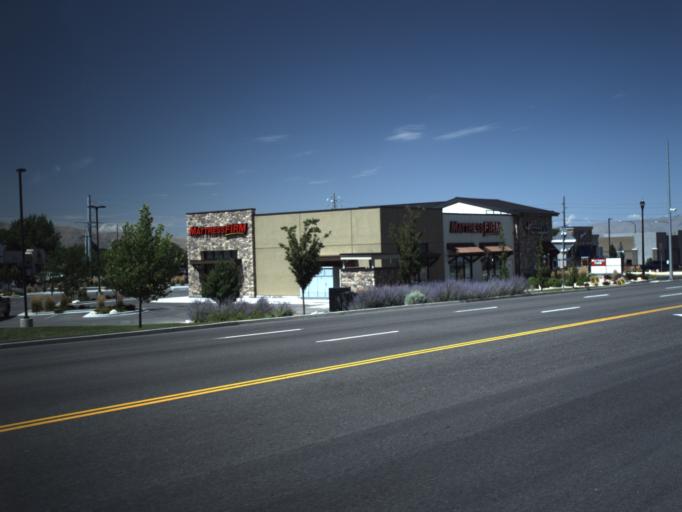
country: US
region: Utah
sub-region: Utah County
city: Spanish Fork
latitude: 40.1216
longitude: -111.6414
